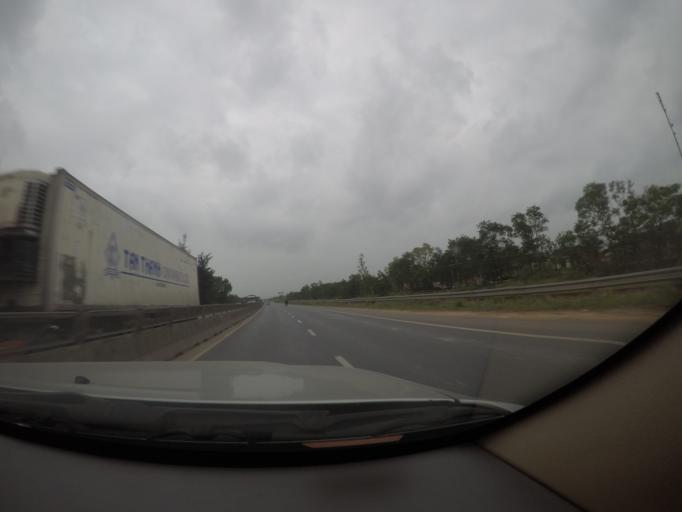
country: VN
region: Quang Tri
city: Hai Lang
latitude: 16.7058
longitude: 107.2220
